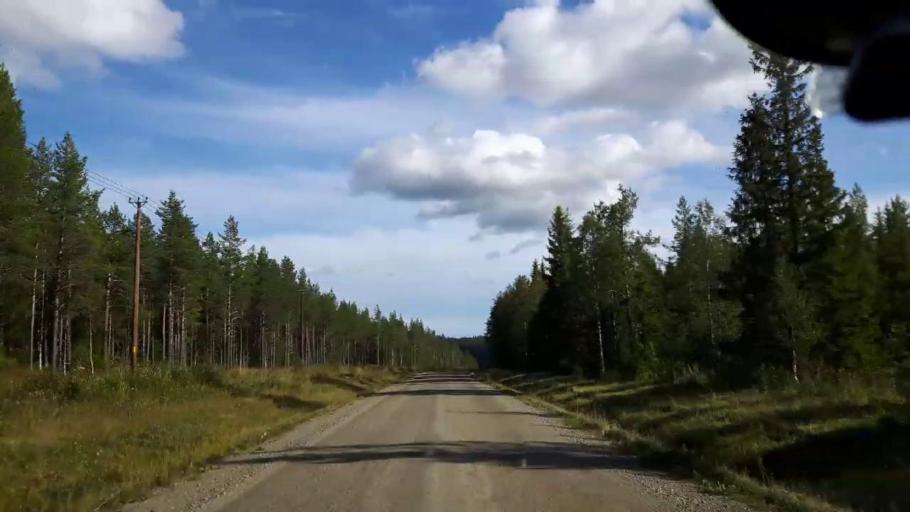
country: SE
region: Jaemtland
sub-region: Ragunda Kommun
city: Hammarstrand
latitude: 63.4293
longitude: 16.0493
